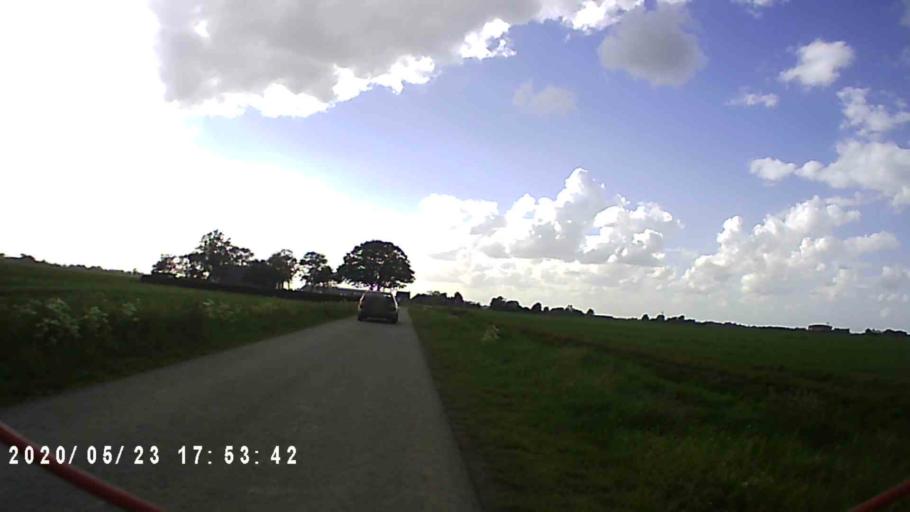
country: NL
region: Groningen
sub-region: Gemeente Slochteren
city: Slochteren
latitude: 53.2451
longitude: 6.7523
